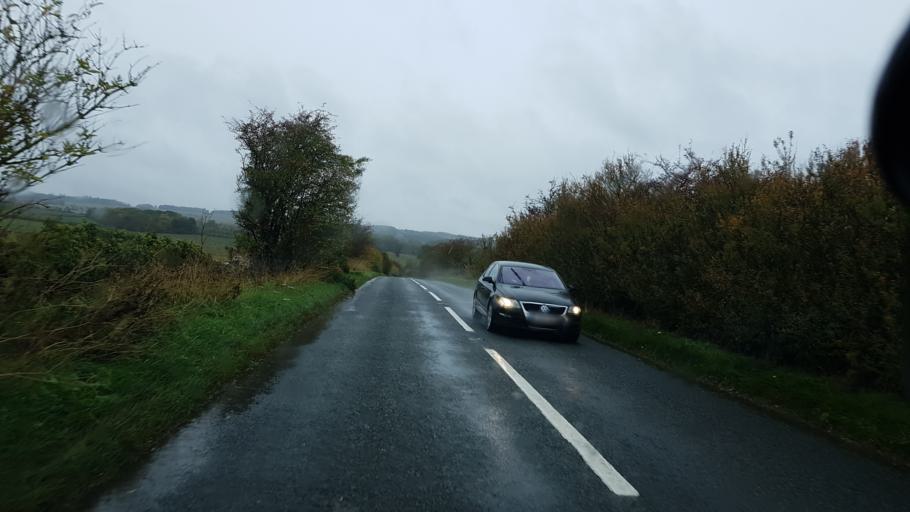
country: GB
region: England
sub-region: Gloucestershire
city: Donnington
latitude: 51.9485
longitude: -1.7914
